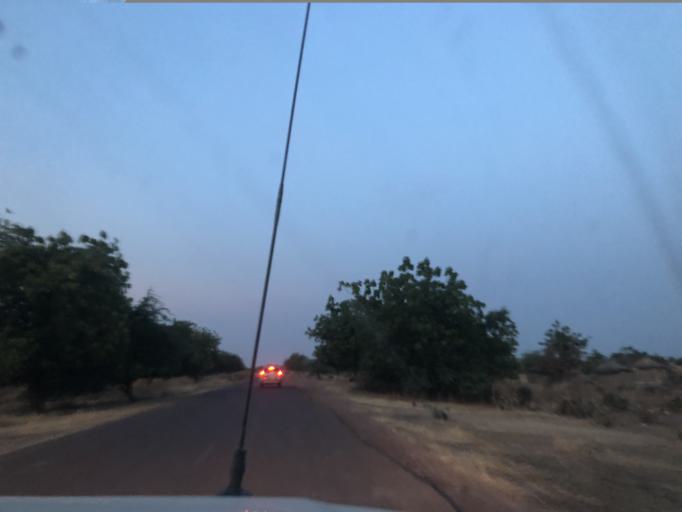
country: TD
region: Mayo-Kebbi Est
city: Guelendeng
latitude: 11.2318
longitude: 15.3690
